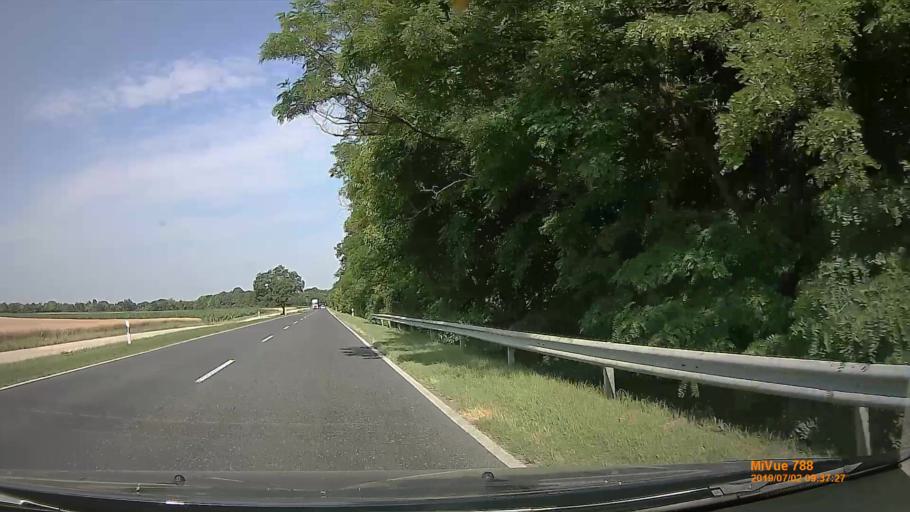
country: HU
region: Gyor-Moson-Sopron
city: Mosonmagyarovar
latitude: 47.8296
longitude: 17.3111
